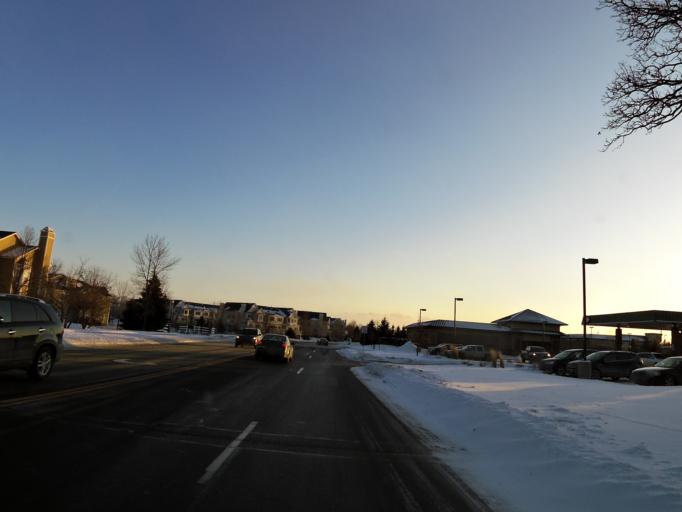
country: US
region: Minnesota
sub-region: Washington County
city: Woodbury
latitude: 44.9197
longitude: -92.9012
